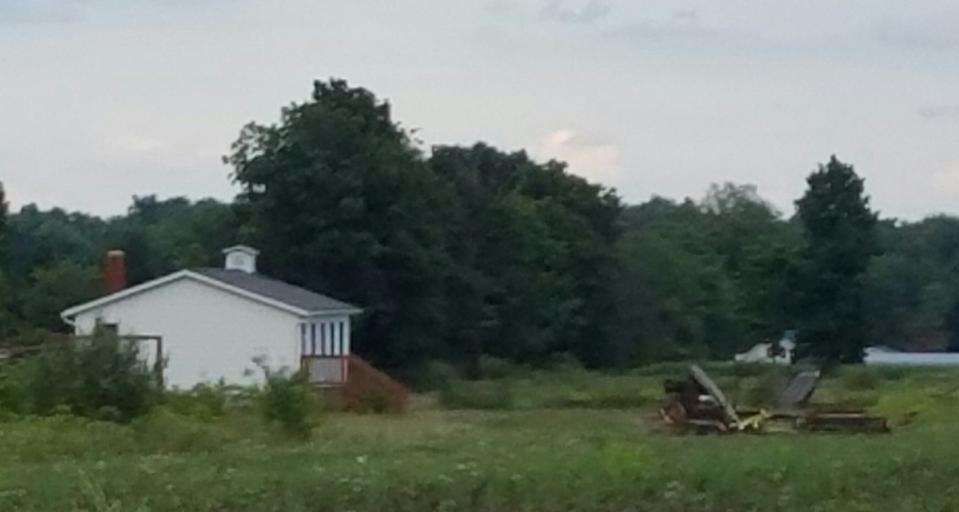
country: US
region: Ohio
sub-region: Richland County
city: Lexington
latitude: 40.6133
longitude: -82.6489
